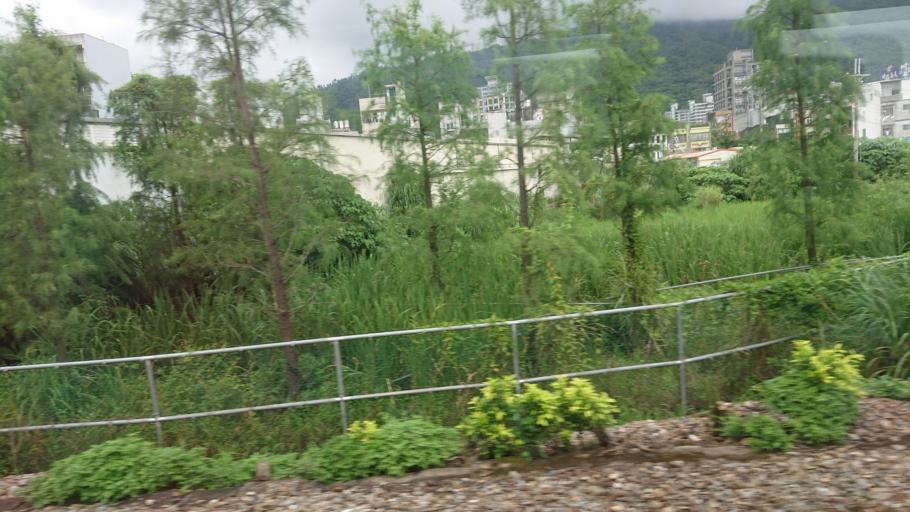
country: TW
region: Taiwan
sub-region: Yilan
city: Yilan
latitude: 24.8244
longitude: 121.7733
